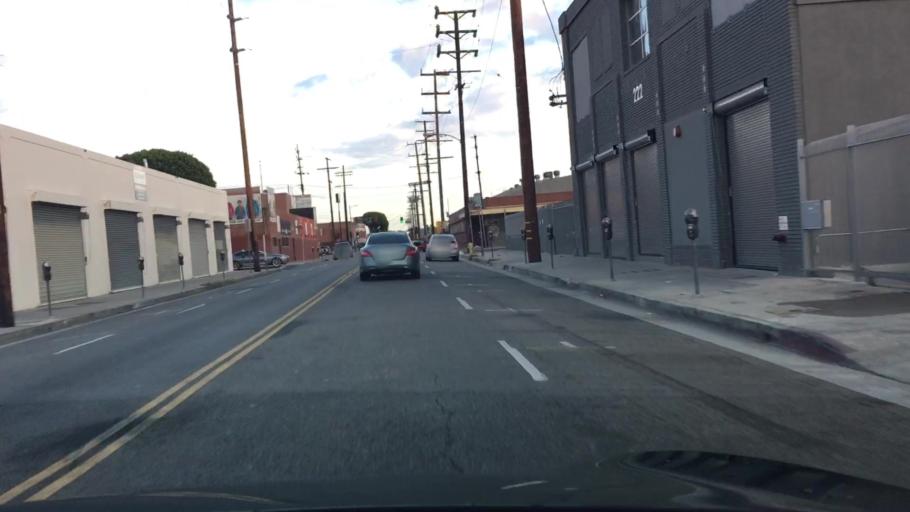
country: US
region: California
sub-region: Los Angeles County
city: Los Angeles
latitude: 34.0328
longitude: -118.2611
